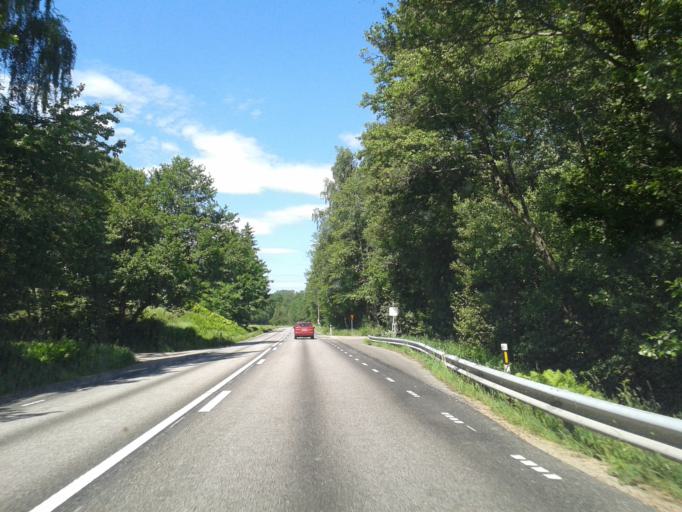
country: SE
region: Vaestra Goetaland
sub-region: Orust
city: Henan
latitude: 58.3171
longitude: 11.6845
